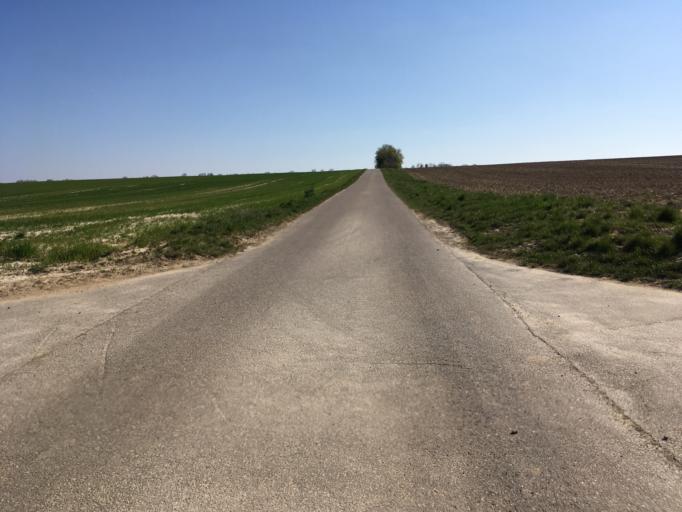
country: DE
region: Baden-Wuerttemberg
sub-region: Regierungsbezirk Stuttgart
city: Massenbachhausen
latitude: 49.1898
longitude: 9.0841
